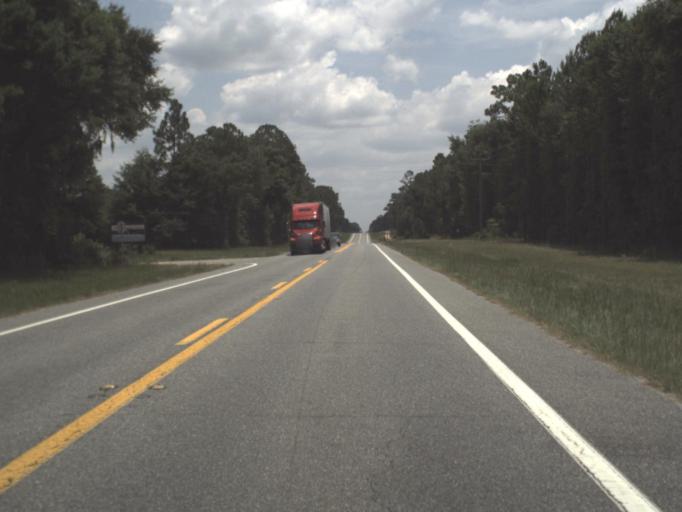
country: US
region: Florida
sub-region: Hamilton County
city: Jasper
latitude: 30.4900
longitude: -83.1500
